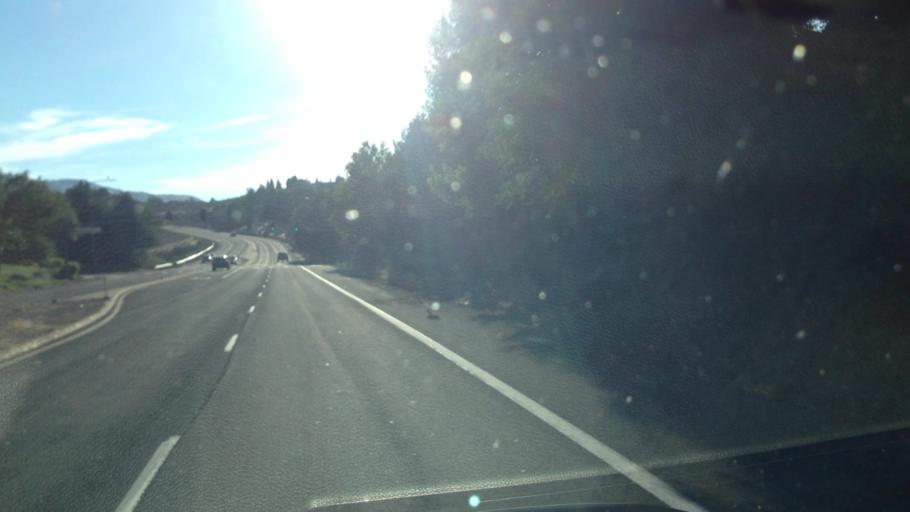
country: US
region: Nevada
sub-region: Washoe County
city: Reno
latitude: 39.4776
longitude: -119.8214
